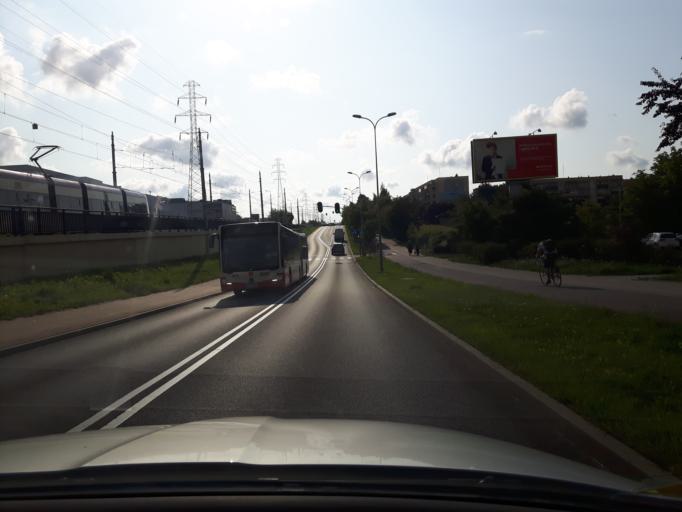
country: PL
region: Pomeranian Voivodeship
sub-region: Gdansk
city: Gdansk
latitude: 54.3381
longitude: 18.6151
